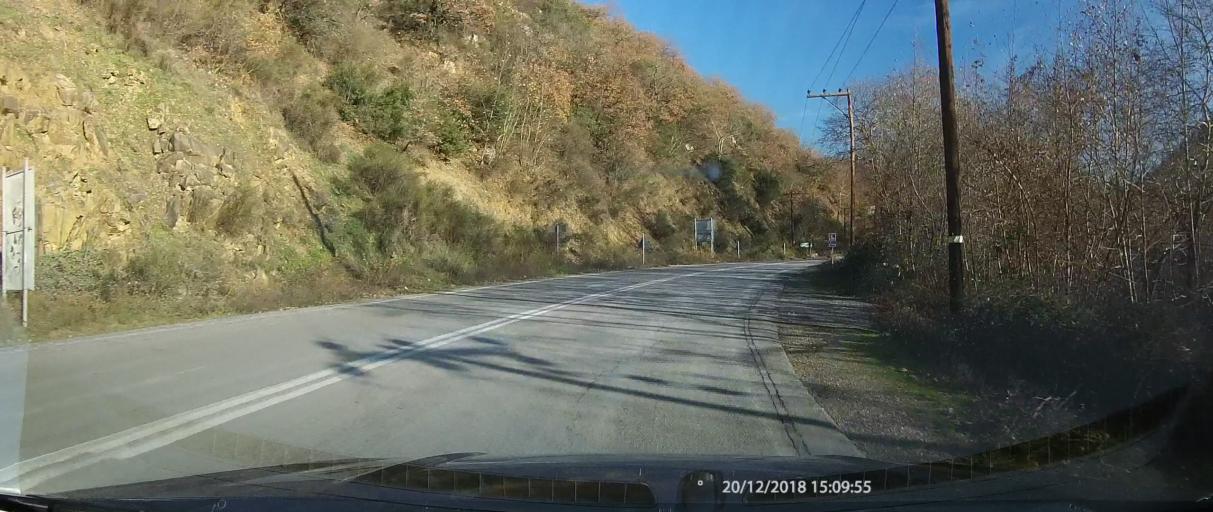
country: GR
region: Central Greece
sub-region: Nomos Evrytanias
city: Karpenisi
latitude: 38.9490
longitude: 21.9472
